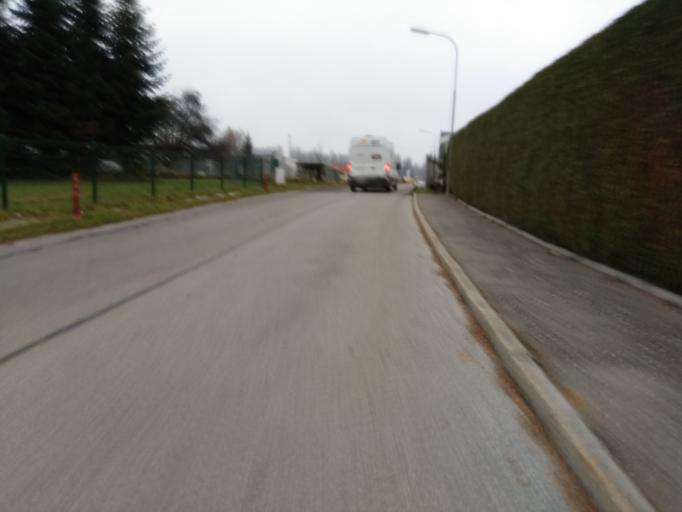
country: AT
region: Styria
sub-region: Politischer Bezirk Bruck-Muerzzuschlag
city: Frauenberg
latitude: 47.4520
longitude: 15.3297
